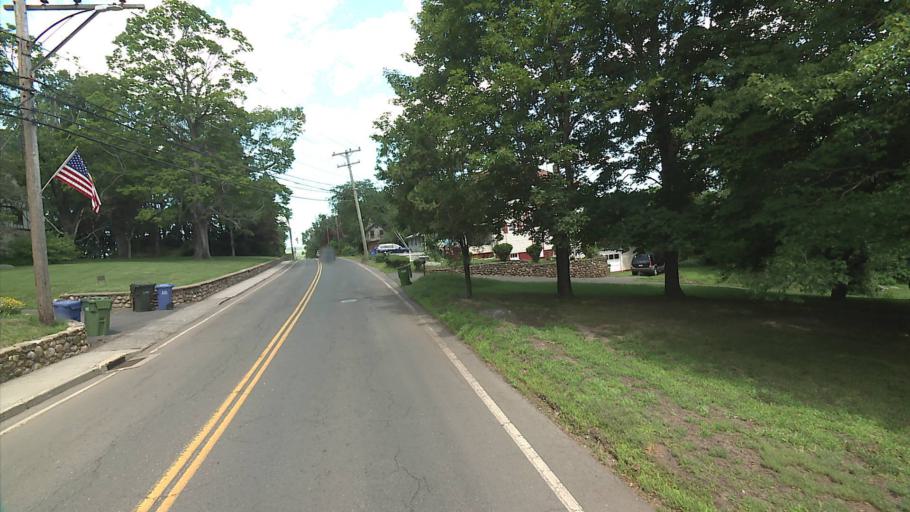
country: US
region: Connecticut
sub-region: Middlesex County
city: East Hampton
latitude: 41.5815
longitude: -72.4966
